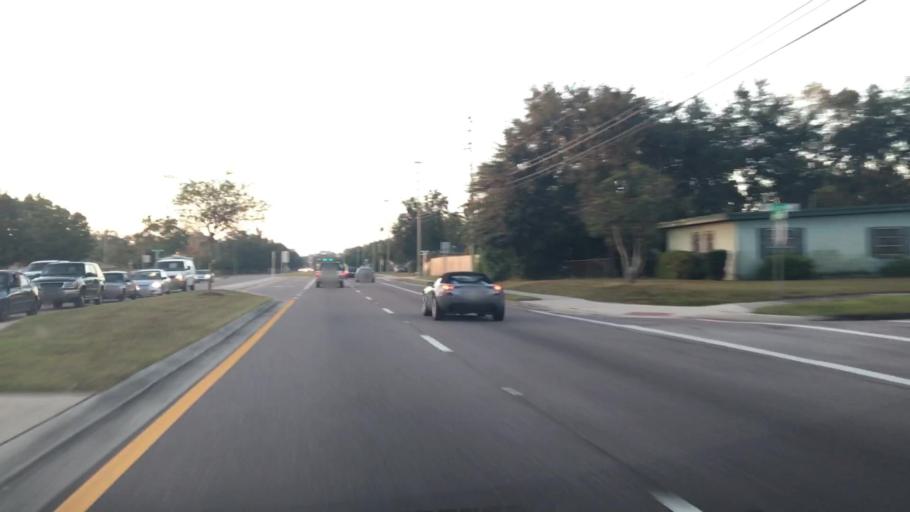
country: US
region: Florida
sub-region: Orange County
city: Azalea Park
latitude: 28.5311
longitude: -81.2857
